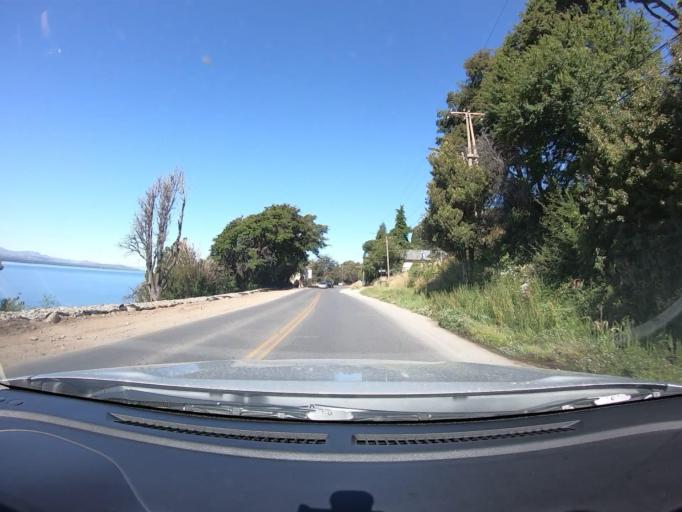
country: AR
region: Rio Negro
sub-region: Departamento de Bariloche
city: San Carlos de Bariloche
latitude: -41.1319
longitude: -71.3365
